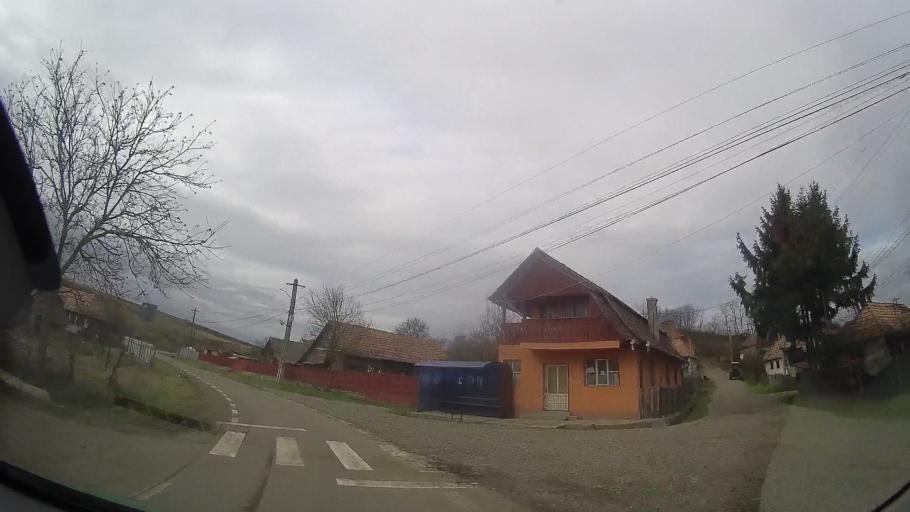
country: RO
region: Mures
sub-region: Comuna Cozma
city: Cozma
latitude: 46.8121
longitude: 24.5111
